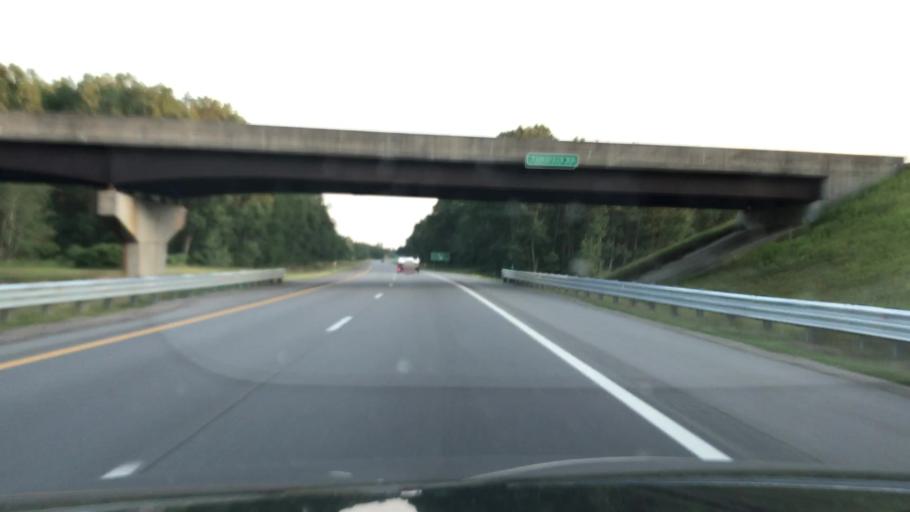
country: US
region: Michigan
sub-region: Montcalm County
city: Howard City
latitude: 43.4396
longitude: -85.4933
